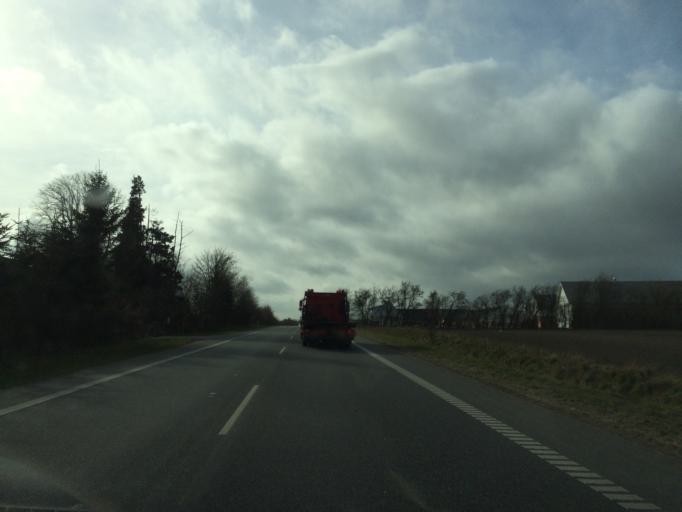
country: DK
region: Central Jutland
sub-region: Randers Kommune
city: Langa
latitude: 56.4758
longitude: 9.9243
